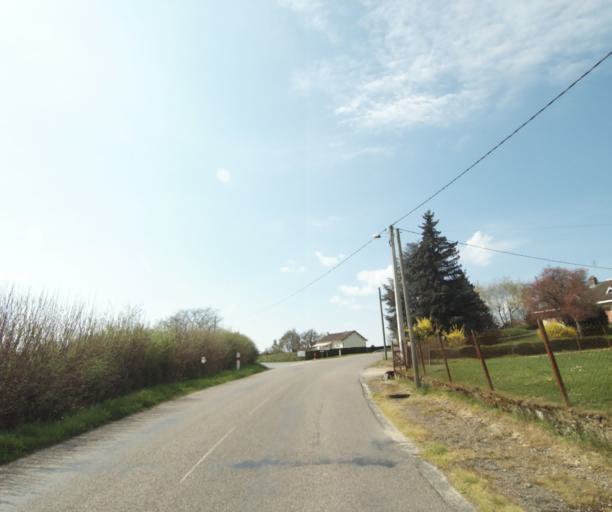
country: FR
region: Bourgogne
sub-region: Departement de Saone-et-Loire
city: Palinges
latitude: 46.5527
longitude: 4.2011
